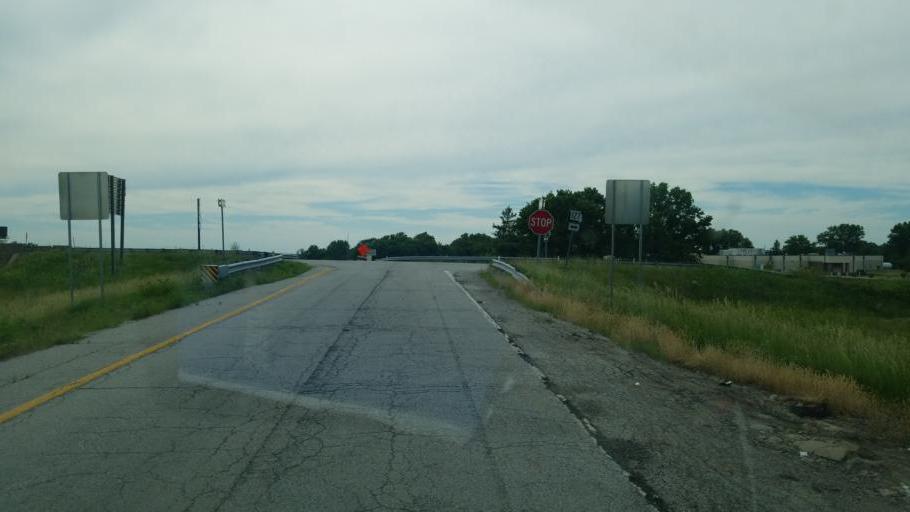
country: US
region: Missouri
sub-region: Saline County
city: Sweet Springs
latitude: 38.9774
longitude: -93.4144
